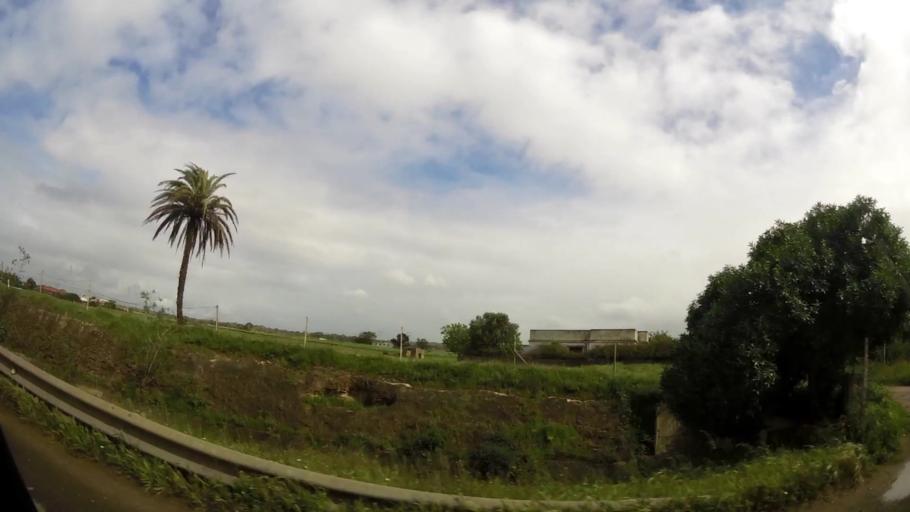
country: MA
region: Grand Casablanca
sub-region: Mohammedia
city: Mohammedia
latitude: 33.6487
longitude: -7.4161
